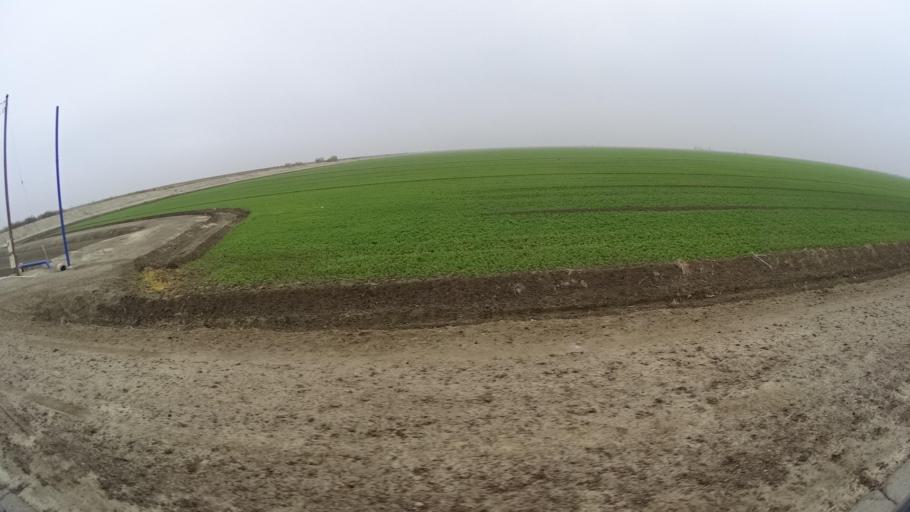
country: US
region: California
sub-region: Kern County
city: Wasco
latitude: 35.6797
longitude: -119.5087
